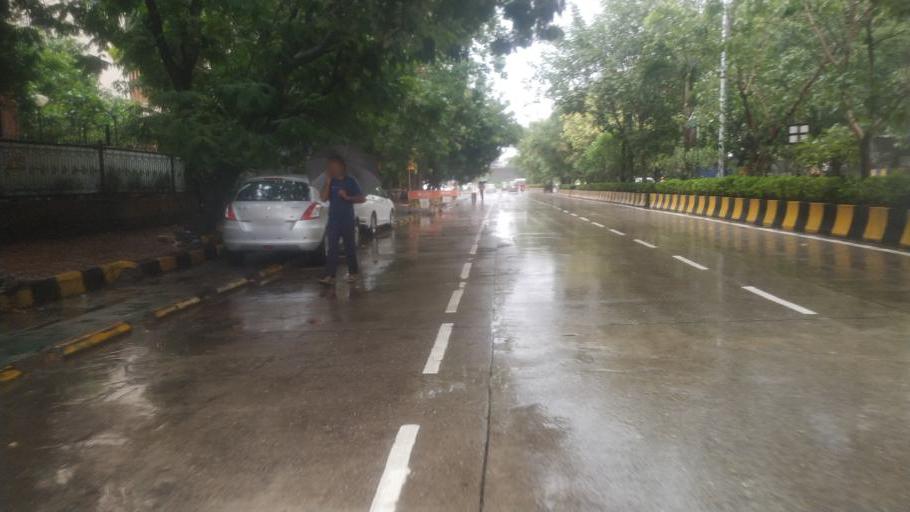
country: IN
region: Maharashtra
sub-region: Mumbai Suburban
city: Mumbai
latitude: 19.0680
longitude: 72.8705
